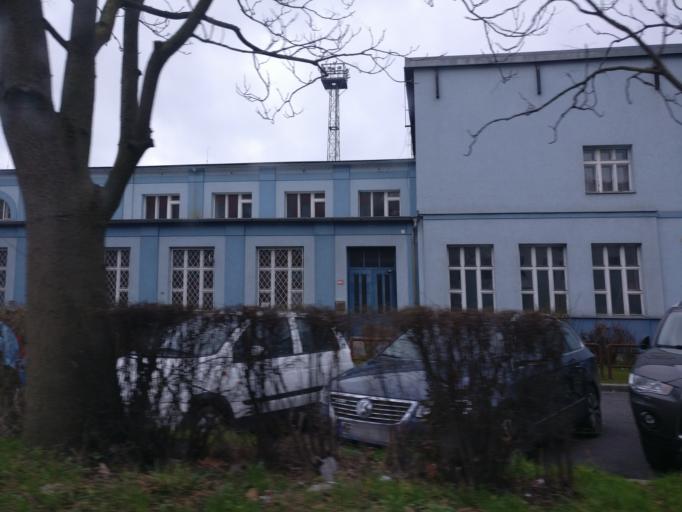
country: CZ
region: Pardubicky
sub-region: Okres Pardubice
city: Pardubice
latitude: 50.0322
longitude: 15.7662
